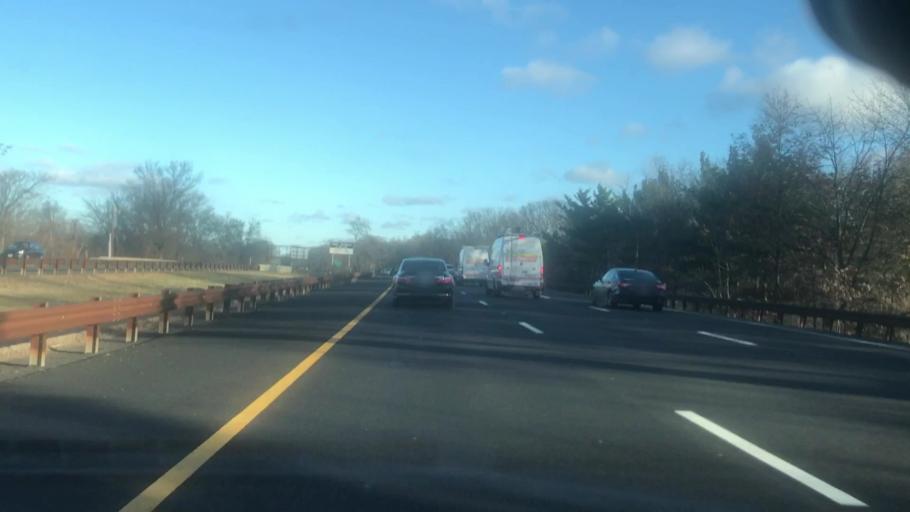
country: US
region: New Jersey
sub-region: Bergen County
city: Paramus
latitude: 40.9472
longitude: -74.0670
